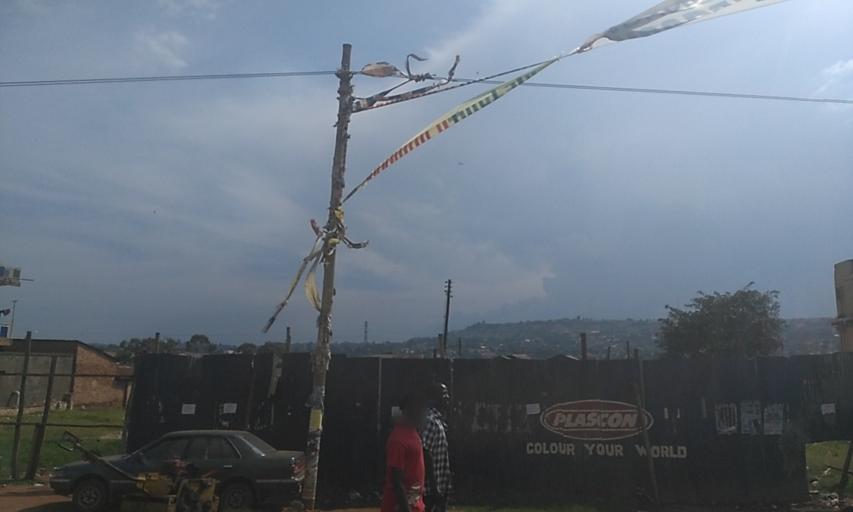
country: UG
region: Central Region
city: Kampala Central Division
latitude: 0.2966
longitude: 32.5427
